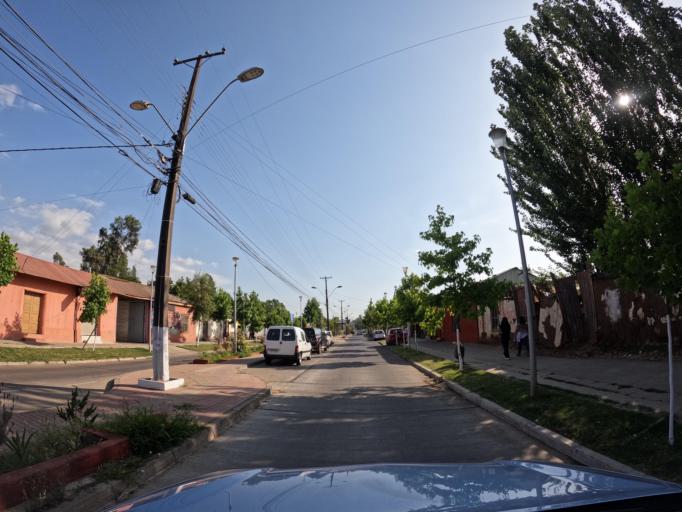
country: CL
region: Maule
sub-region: Provincia de Curico
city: Molina
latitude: -35.2856
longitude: -71.2615
